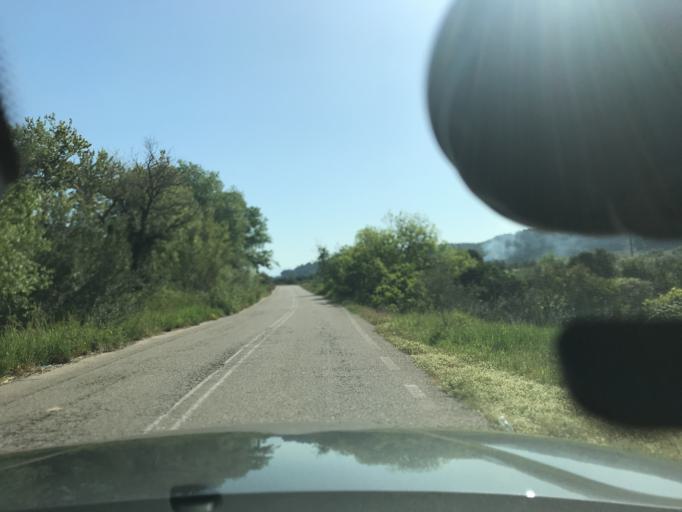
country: GR
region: West Greece
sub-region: Nomos Ileias
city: Epitalion
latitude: 37.6402
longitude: 21.4897
